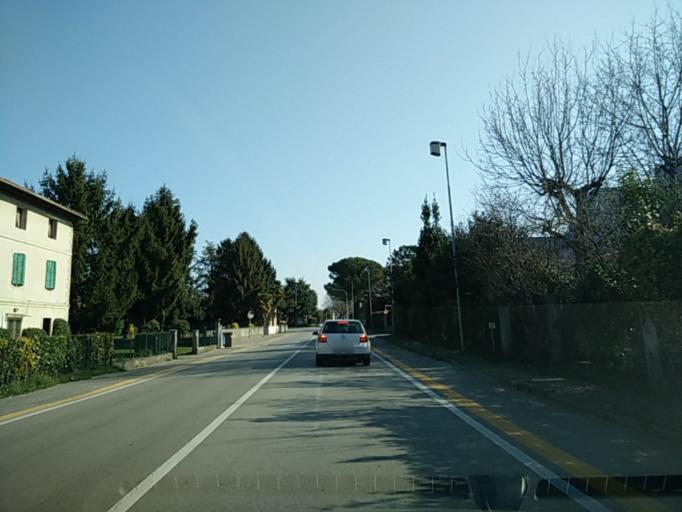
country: IT
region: Friuli Venezia Giulia
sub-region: Provincia di Pordenone
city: San Vito al Tagliamento
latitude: 45.9107
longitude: 12.8453
